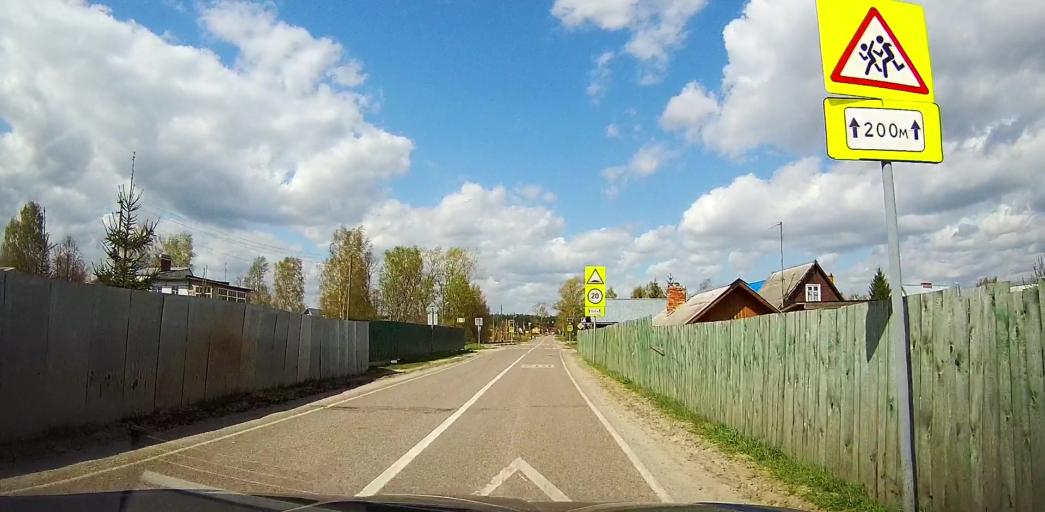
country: RU
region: Moskovskaya
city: Davydovo
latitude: 55.5554
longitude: 38.8149
